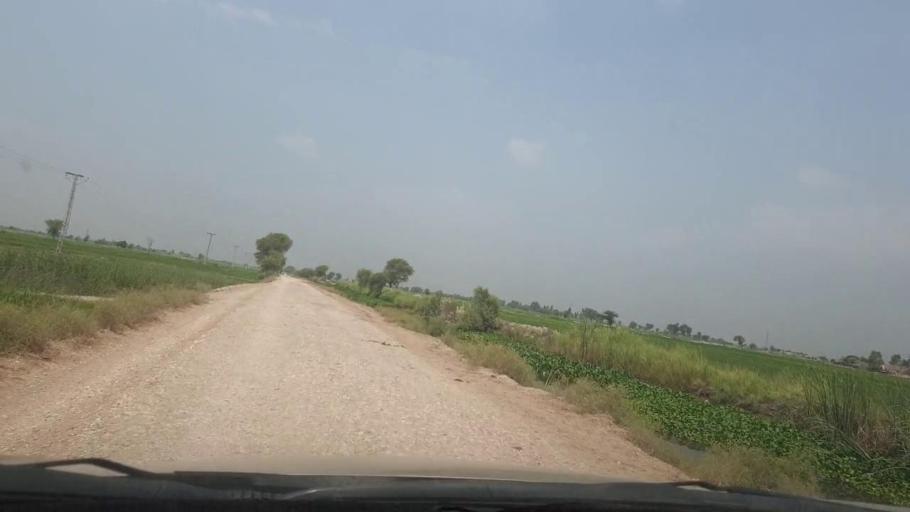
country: PK
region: Sindh
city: Naudero
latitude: 27.6874
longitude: 68.2601
